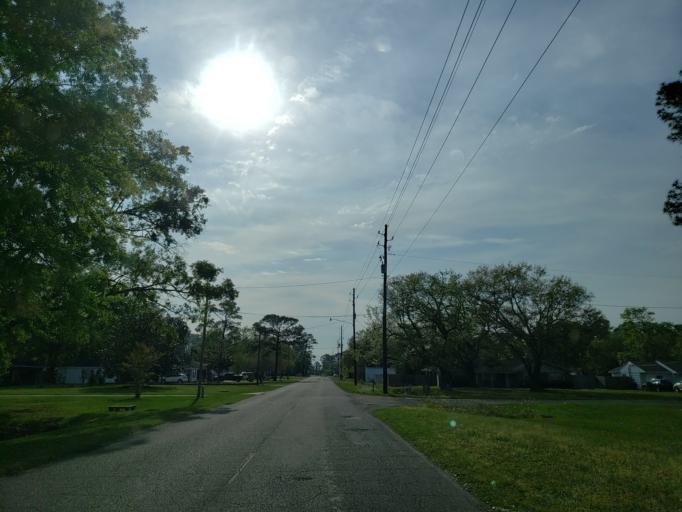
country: US
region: Mississippi
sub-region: Harrison County
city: West Gulfport
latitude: 30.4093
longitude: -89.0476
